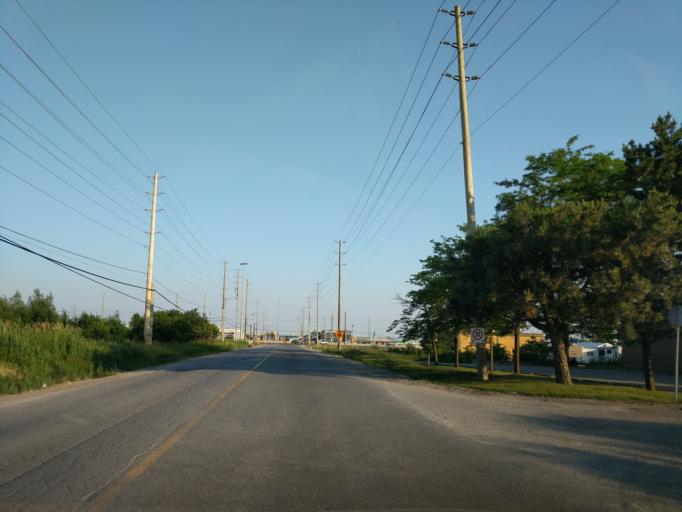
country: CA
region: Ontario
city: Oshawa
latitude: 43.8760
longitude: -78.8862
